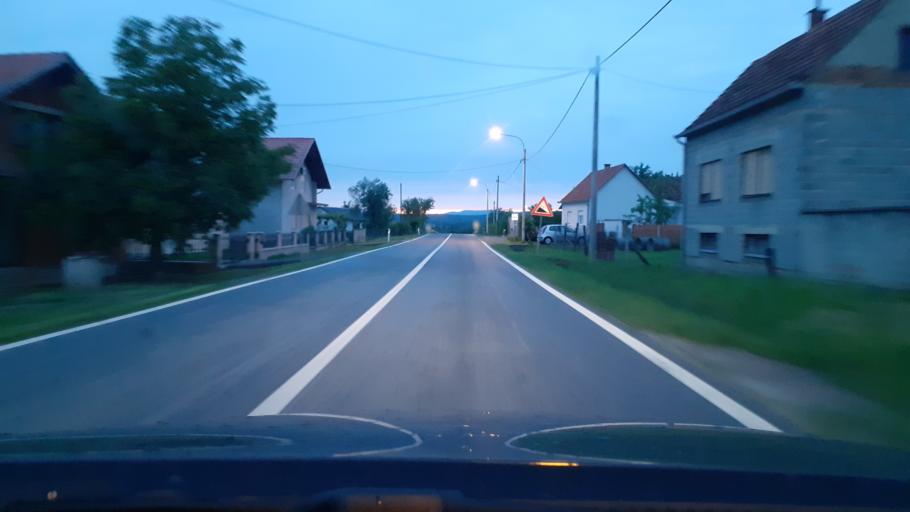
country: HR
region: Pozesko-Slavonska
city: Bilice
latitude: 45.2375
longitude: 17.8406
